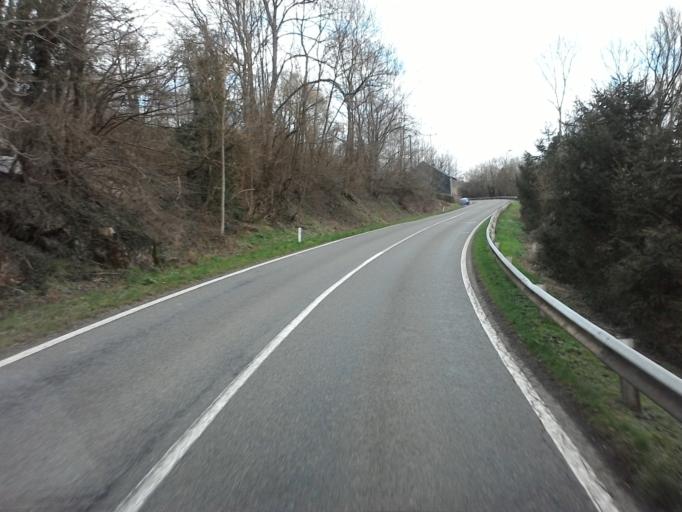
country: BE
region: Wallonia
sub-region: Province de Liege
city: Ferrieres
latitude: 50.4040
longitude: 5.6083
